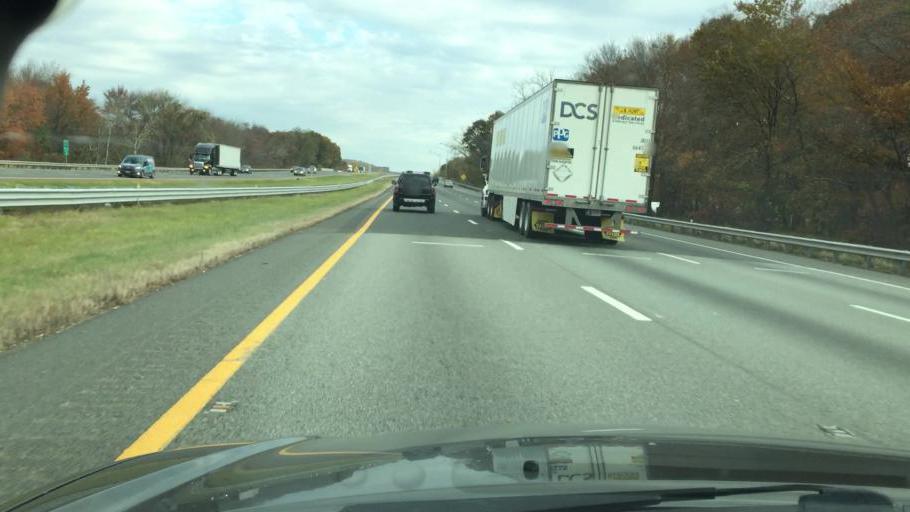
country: US
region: New Jersey
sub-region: Morris County
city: Kenvil
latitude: 40.9035
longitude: -74.6141
